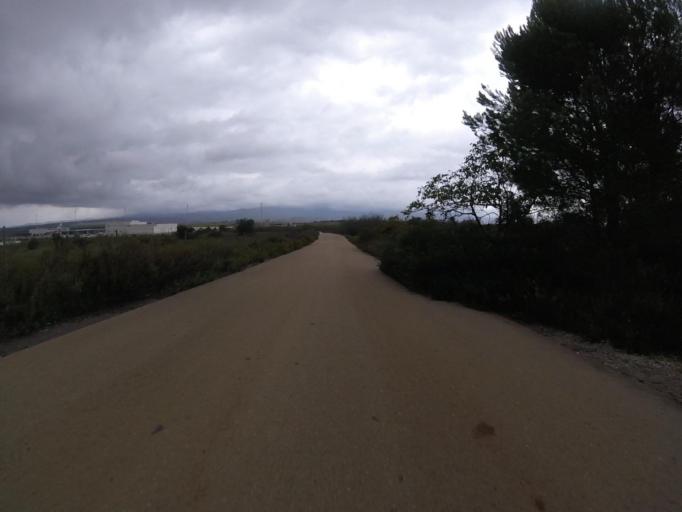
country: ES
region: Valencia
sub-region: Provincia de Castello
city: Benlloch
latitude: 40.2044
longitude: 0.0720
